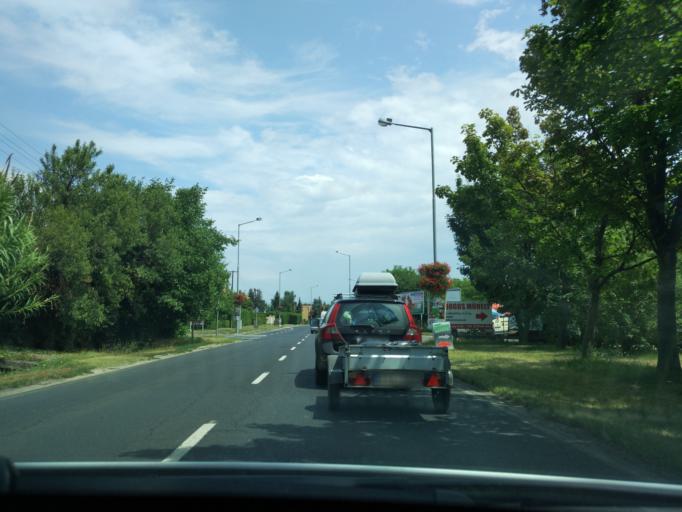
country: HU
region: Veszprem
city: Csopak
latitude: 46.9852
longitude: 17.9718
